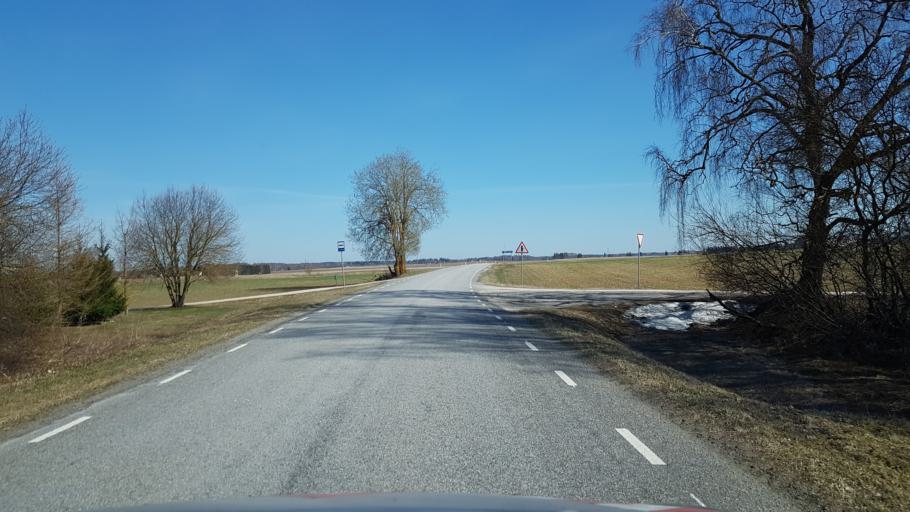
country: EE
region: Laeaene-Virumaa
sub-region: Vinni vald
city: Vinni
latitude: 59.2786
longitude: 26.3847
